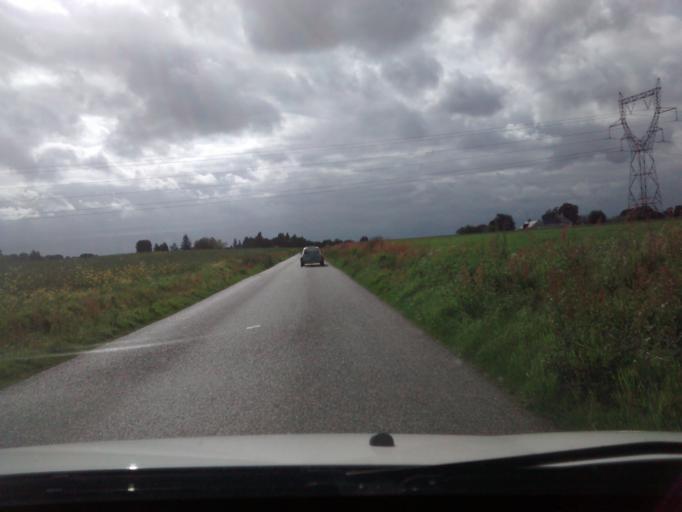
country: FR
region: Brittany
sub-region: Departement d'Ille-et-Vilaine
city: Nouvoitou
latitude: 48.0696
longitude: -1.5360
